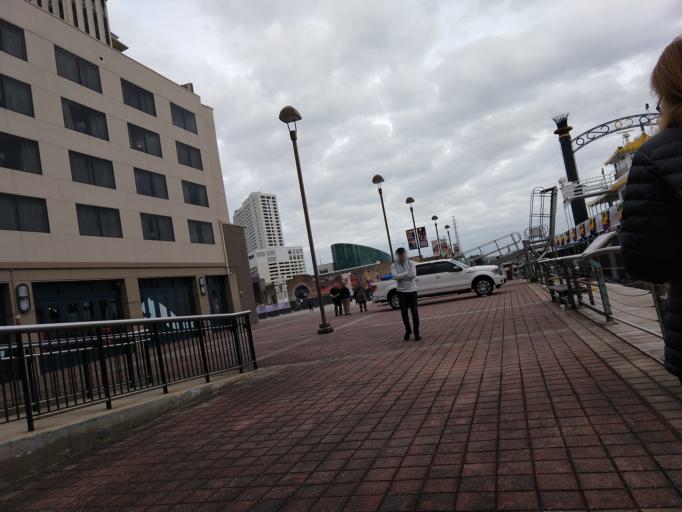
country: US
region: Louisiana
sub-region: Orleans Parish
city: New Orleans
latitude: 29.9481
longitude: -90.0620
